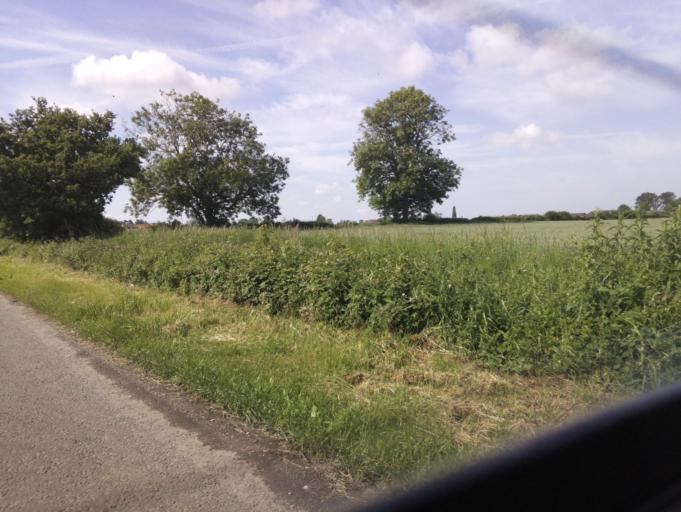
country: GB
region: England
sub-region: Lincolnshire
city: Skellingthorpe
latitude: 53.1377
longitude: -0.6324
